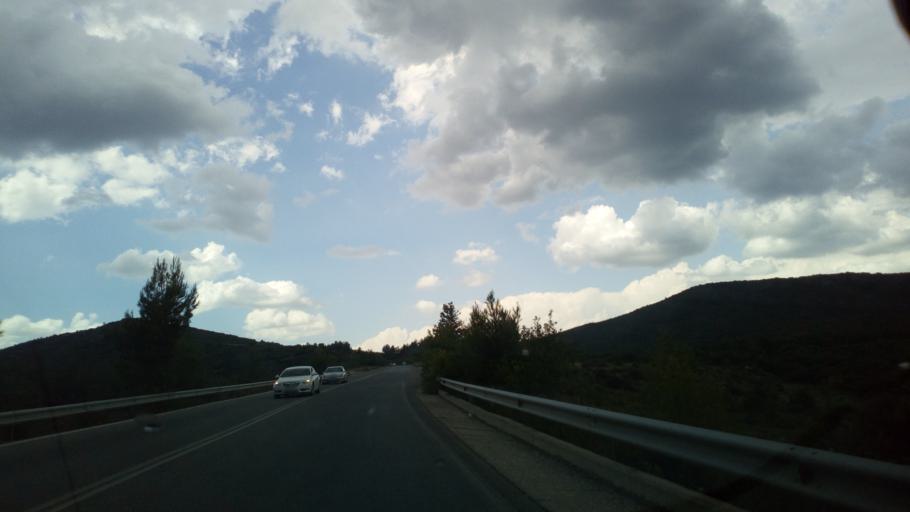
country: GR
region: Central Macedonia
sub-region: Nomos Chalkidikis
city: Polygyros
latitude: 40.3474
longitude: 23.4488
